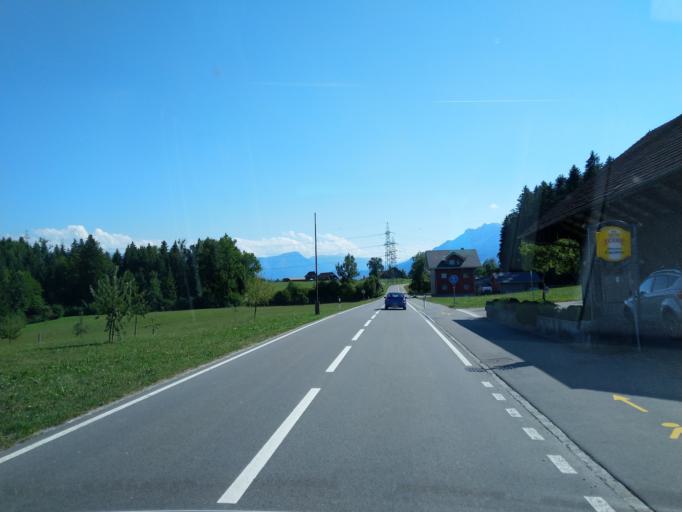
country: CH
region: Lucerne
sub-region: Hochdorf District
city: Emmen
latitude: 47.1139
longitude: 8.2916
